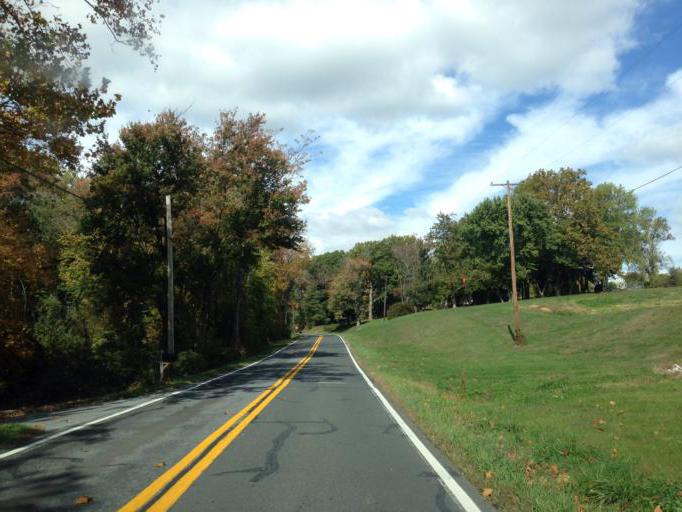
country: US
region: Maryland
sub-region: Carroll County
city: Mount Airy
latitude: 39.3636
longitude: -77.1392
